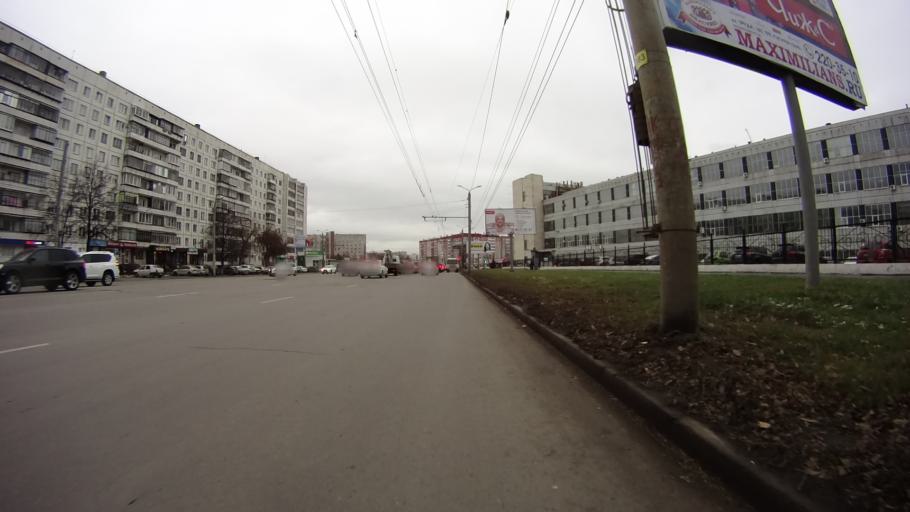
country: RU
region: Chelyabinsk
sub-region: Gorod Chelyabinsk
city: Chelyabinsk
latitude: 55.1930
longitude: 61.3588
